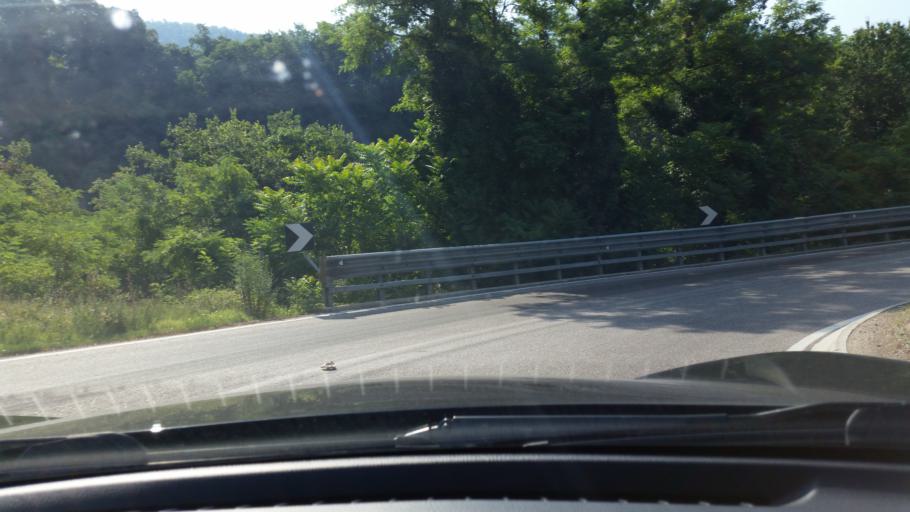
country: IT
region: Trentino-Alto Adige
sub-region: Bolzano
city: Ora
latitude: 46.3409
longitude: 11.2981
